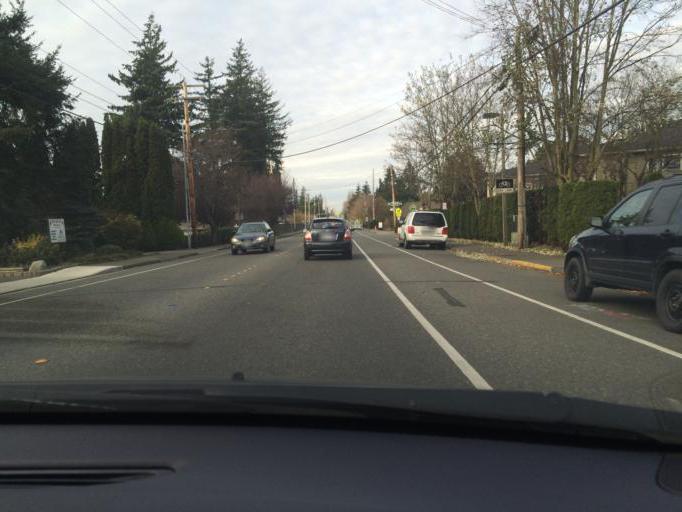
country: US
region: Washington
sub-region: Whatcom County
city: Bellingham
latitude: 48.7776
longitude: -122.4987
